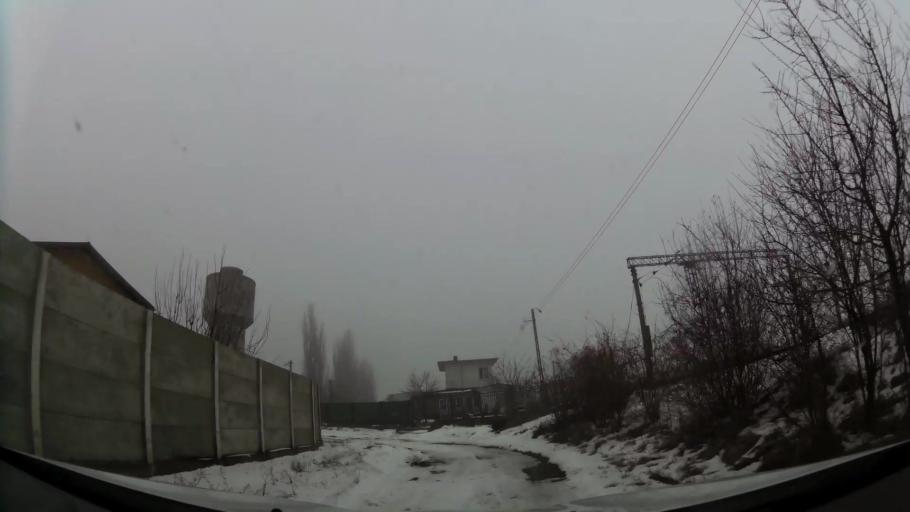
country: RO
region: Ilfov
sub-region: Comuna Chitila
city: Rudeni
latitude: 44.4671
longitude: 25.9763
